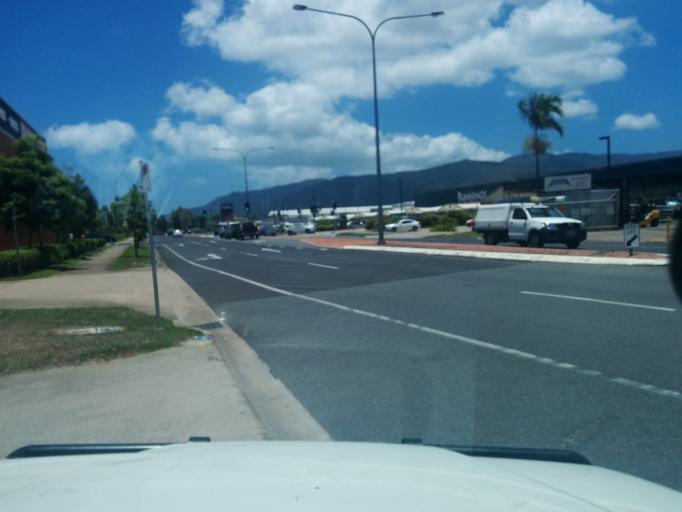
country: AU
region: Queensland
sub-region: Cairns
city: Cairns
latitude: -16.9341
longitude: 145.7717
